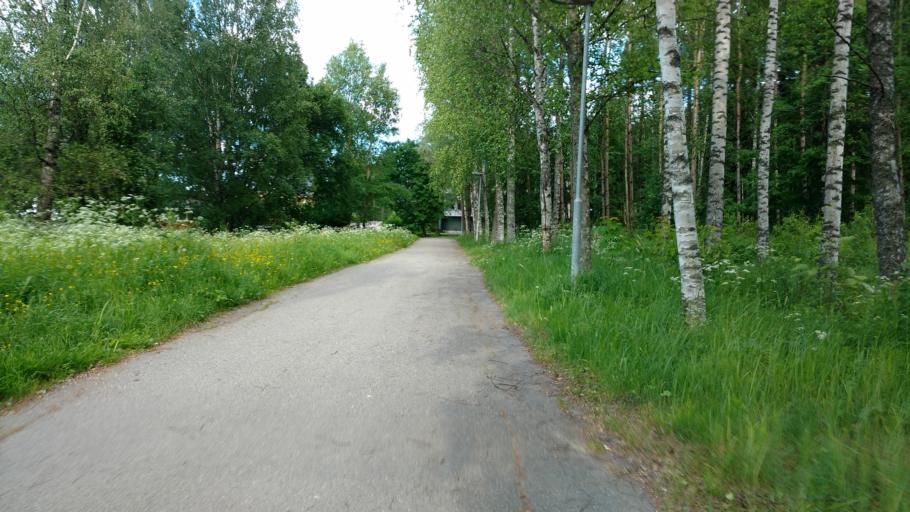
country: FI
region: Varsinais-Suomi
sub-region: Salo
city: Salo
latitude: 60.3861
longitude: 23.1527
